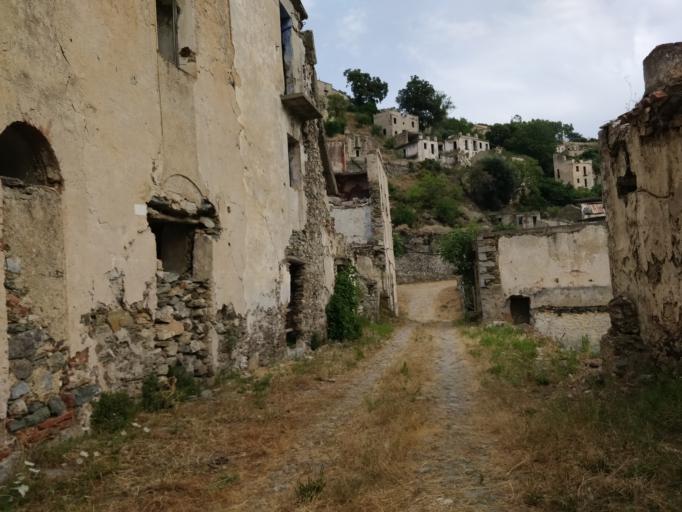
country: IT
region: Sardinia
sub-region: Provincia di Ogliastra
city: Gairo Sant'Elena
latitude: 39.8482
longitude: 9.4986
